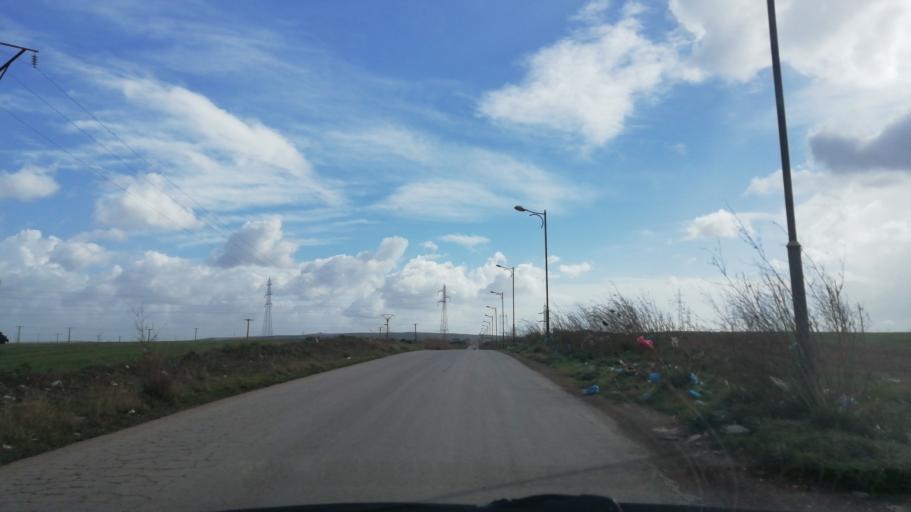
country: DZ
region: Oran
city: Sidi ech Chahmi
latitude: 35.6369
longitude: -0.5466
